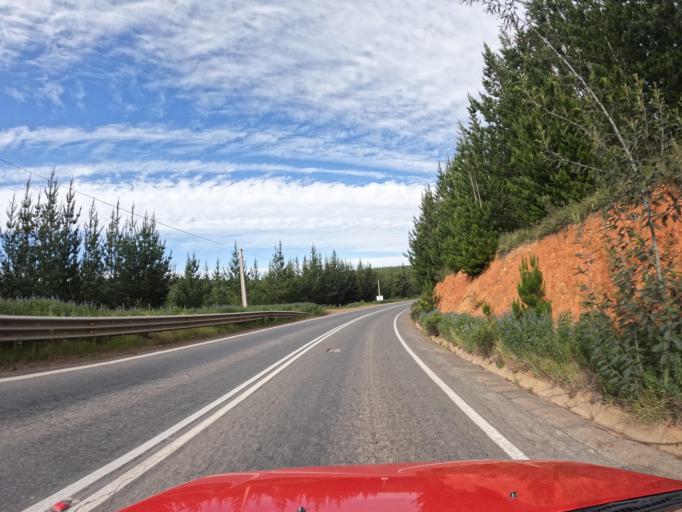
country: CL
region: O'Higgins
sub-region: Provincia de Colchagua
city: Santa Cruz
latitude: -34.3136
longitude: -71.8605
